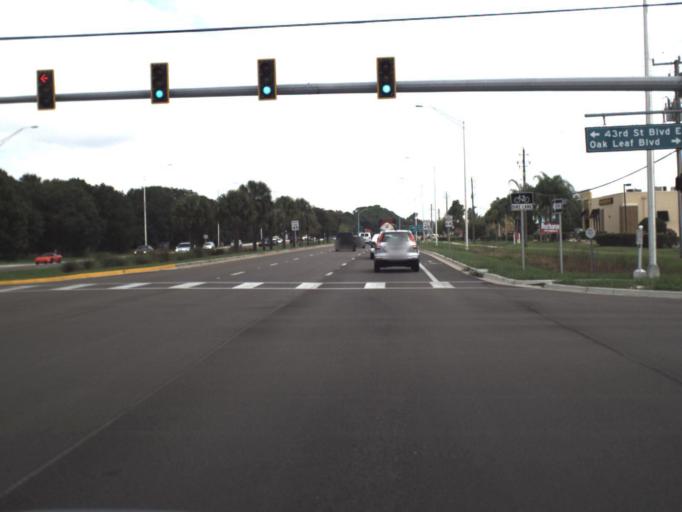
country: US
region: Florida
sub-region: Manatee County
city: Ellenton
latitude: 27.4983
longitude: -82.5089
